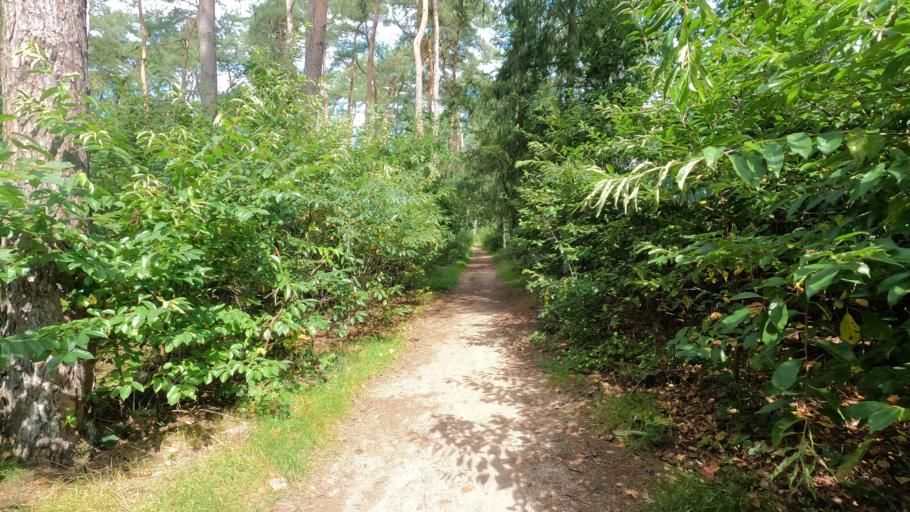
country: BE
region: Flanders
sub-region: Provincie Antwerpen
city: Zoersel
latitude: 51.2540
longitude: 4.7488
